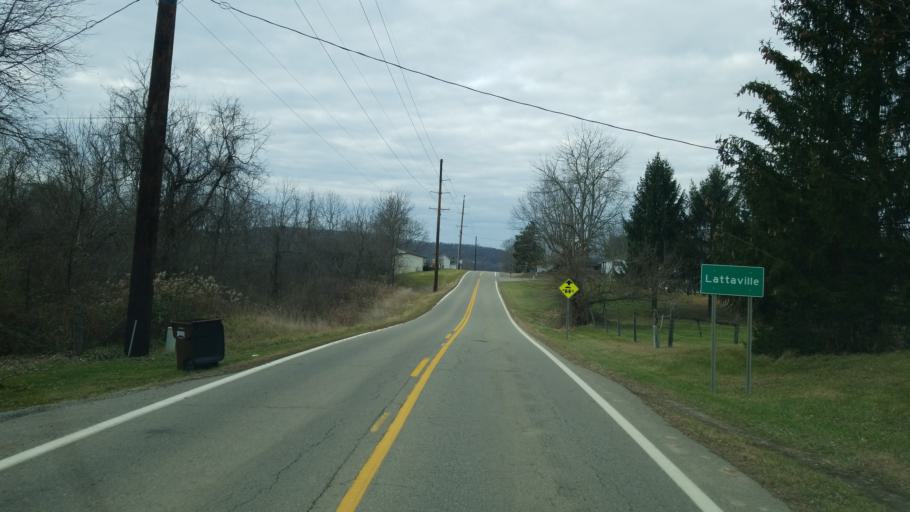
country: US
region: Ohio
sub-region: Ross County
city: Frankfort
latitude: 39.3479
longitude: -83.1998
